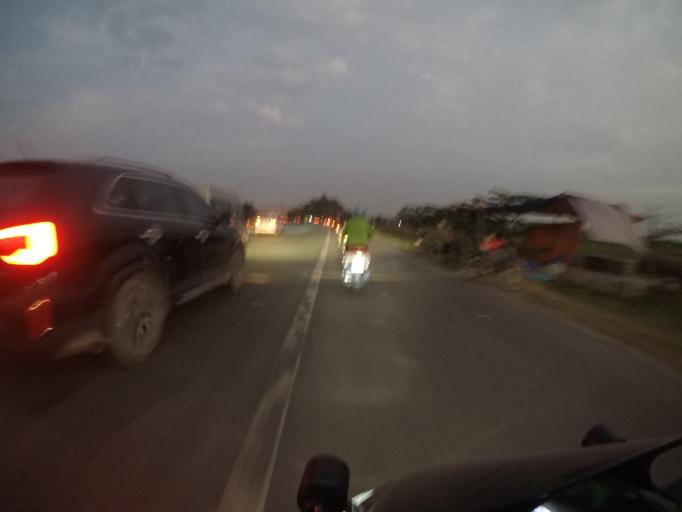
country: VN
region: Vinh Phuc
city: Phuc Yen
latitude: 21.2336
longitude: 105.7497
